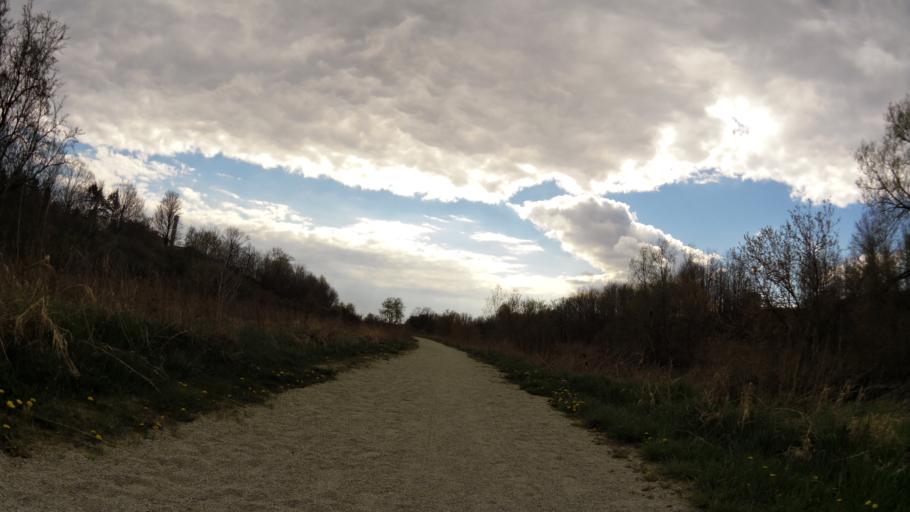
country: CA
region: Ontario
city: Etobicoke
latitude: 43.6730
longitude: -79.6495
